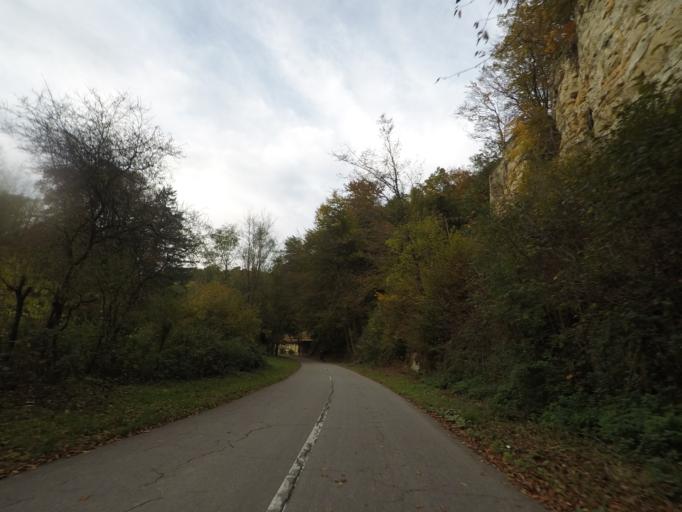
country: LU
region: Luxembourg
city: Itzig
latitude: 49.6043
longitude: 6.1705
